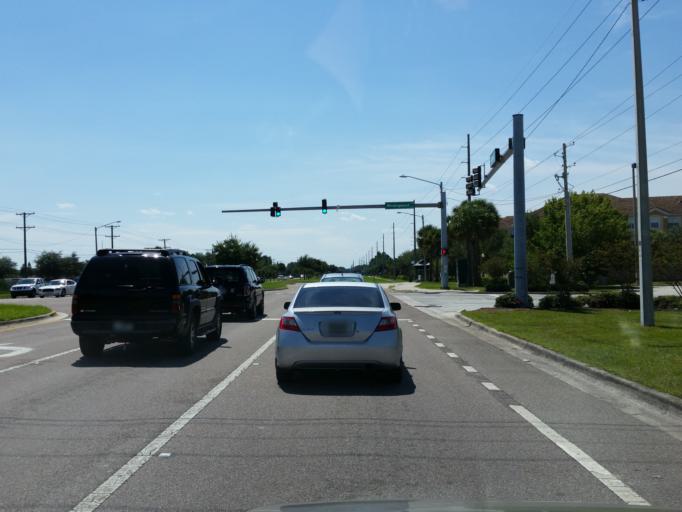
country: US
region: Florida
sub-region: Hillsborough County
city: Brandon
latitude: 27.9206
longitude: -82.3188
